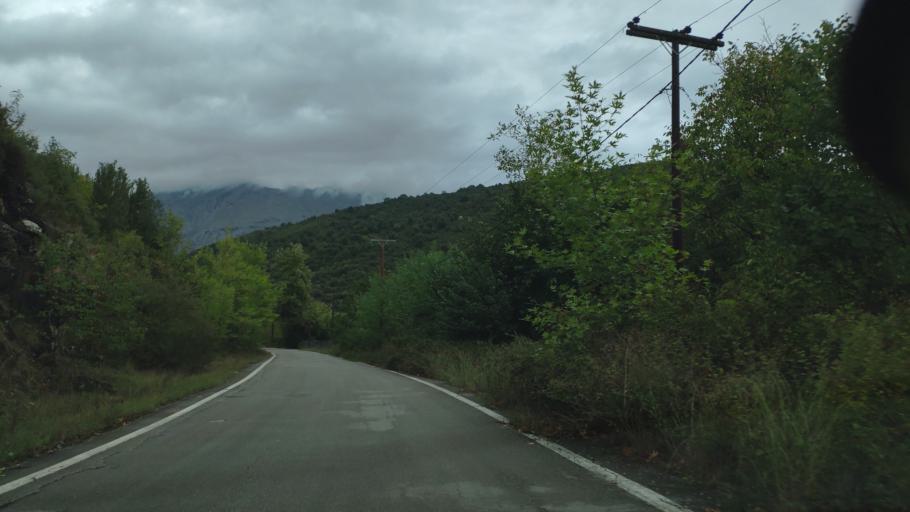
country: GR
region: West Greece
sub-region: Nomos Aitolias kai Akarnanias
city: Sardinia
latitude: 38.9494
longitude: 21.3411
